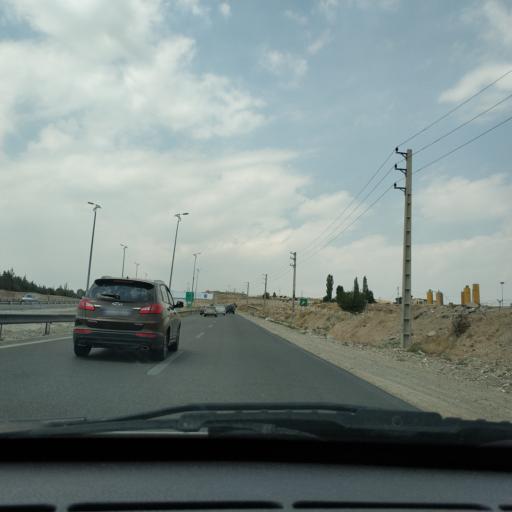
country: IR
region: Tehran
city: Tajrish
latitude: 35.7821
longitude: 51.5640
